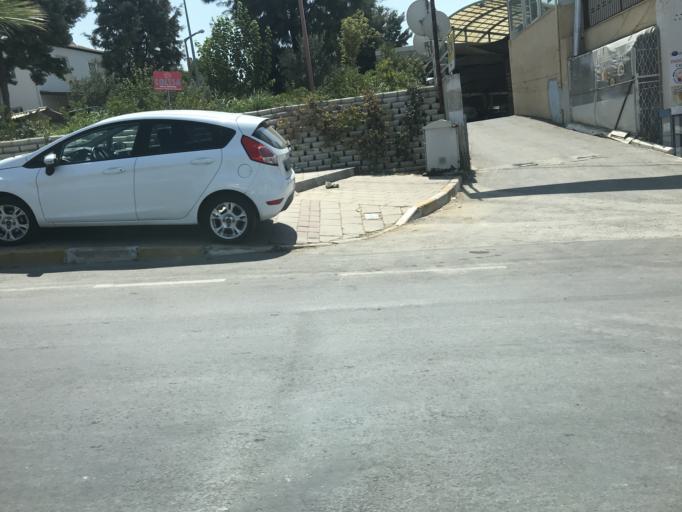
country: TR
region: Izmir
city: Urla
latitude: 38.3260
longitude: 26.7548
